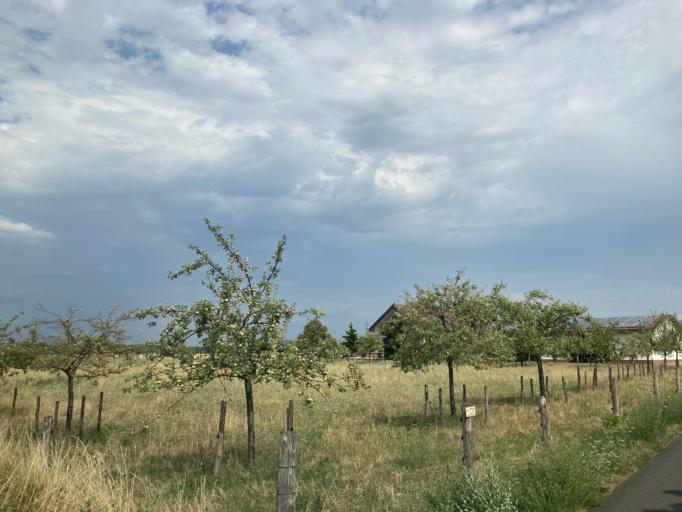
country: DE
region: Hesse
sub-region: Regierungsbezirk Darmstadt
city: Trebur
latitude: 49.9291
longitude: 8.4155
